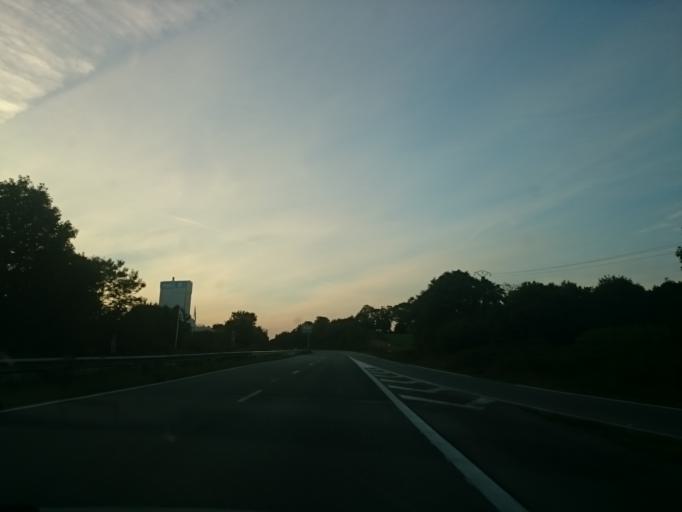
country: FR
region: Brittany
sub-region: Departement du Finistere
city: Ergue-Gaberic
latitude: 47.9798
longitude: -4.0124
